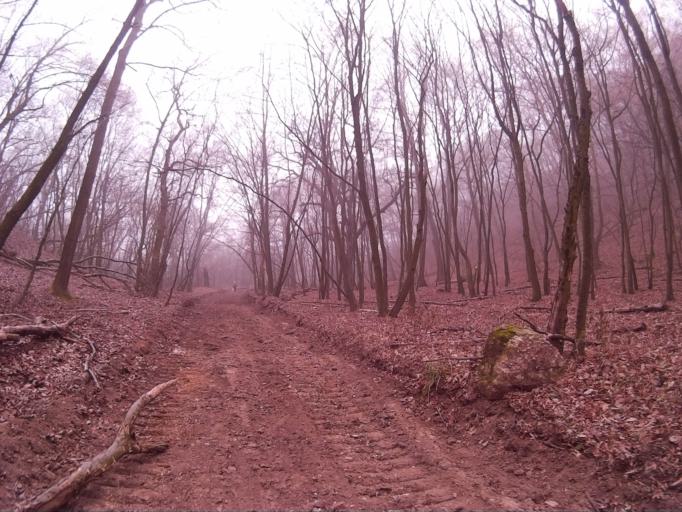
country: HU
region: Komarom-Esztergom
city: Oroszlany
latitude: 47.4497
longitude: 18.3936
